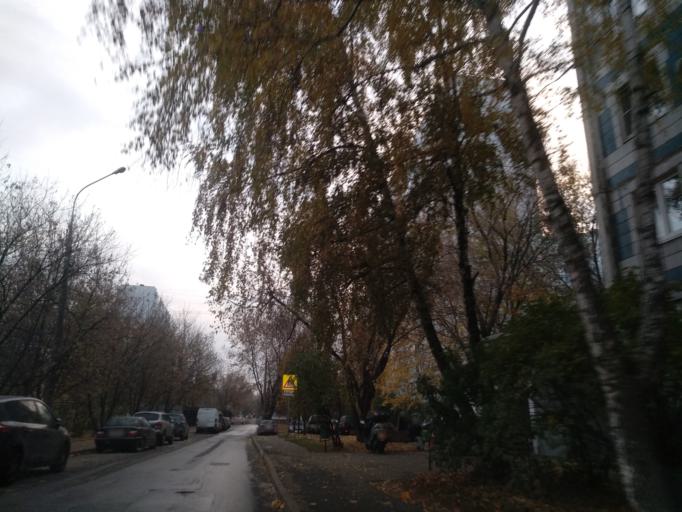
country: RU
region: Moscow
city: Leonovo
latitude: 55.8674
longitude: 37.6567
